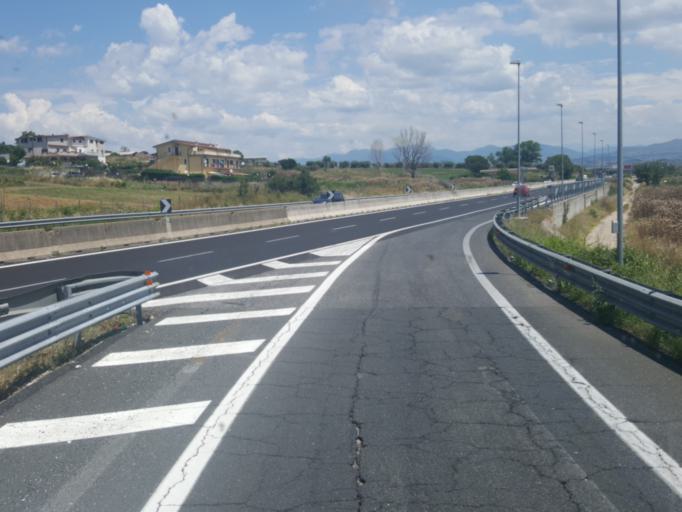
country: IT
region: Latium
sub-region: Citta metropolitana di Roma Capitale
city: Fiano Romano
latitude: 42.1419
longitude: 12.6126
